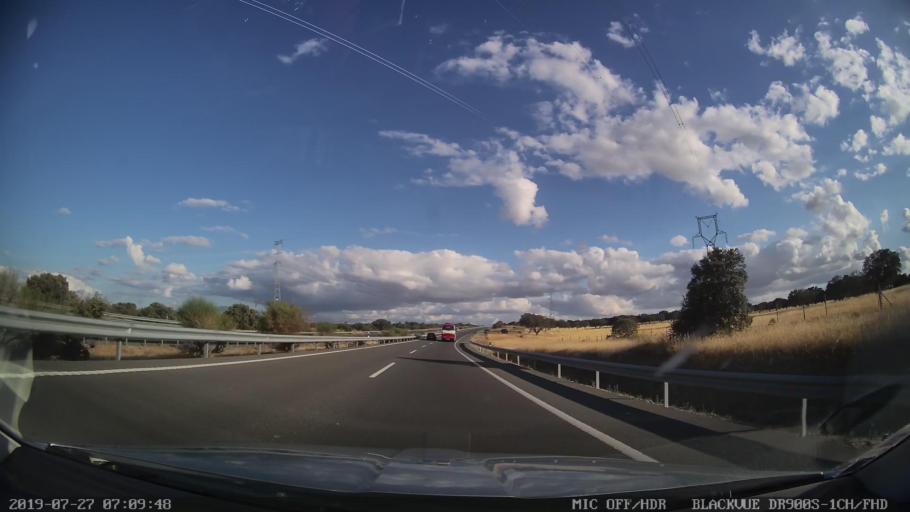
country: ES
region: Extremadura
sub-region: Provincia de Caceres
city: Jaraicejo
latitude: 39.5874
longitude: -5.8354
